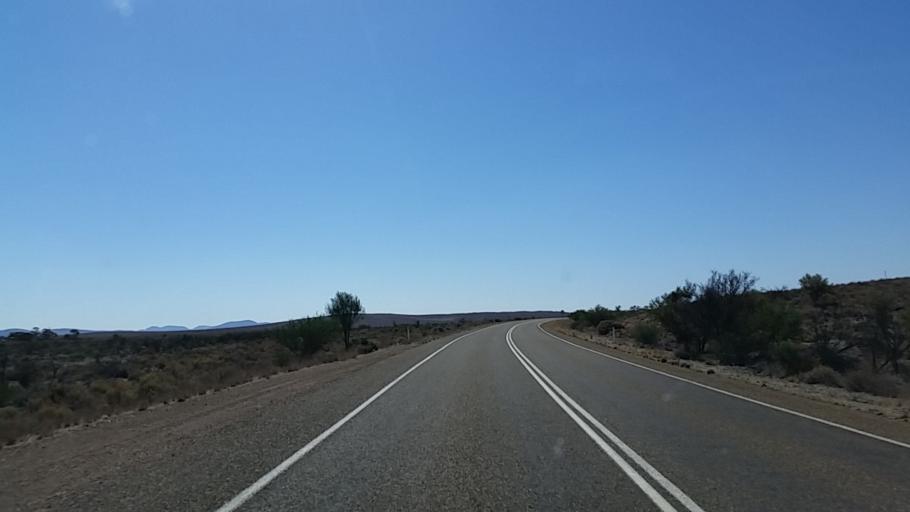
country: AU
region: South Australia
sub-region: Flinders Ranges
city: Quorn
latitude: -32.1074
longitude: 138.5025
